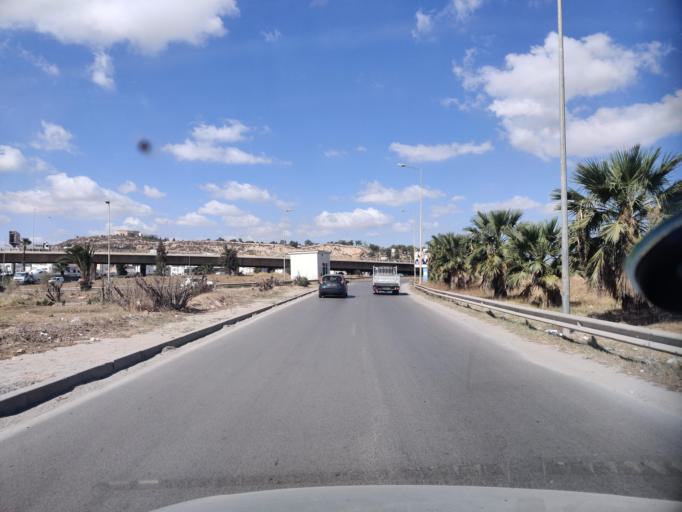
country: TN
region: Bin 'Arus
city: Ben Arous
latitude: 36.7814
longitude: 10.1991
